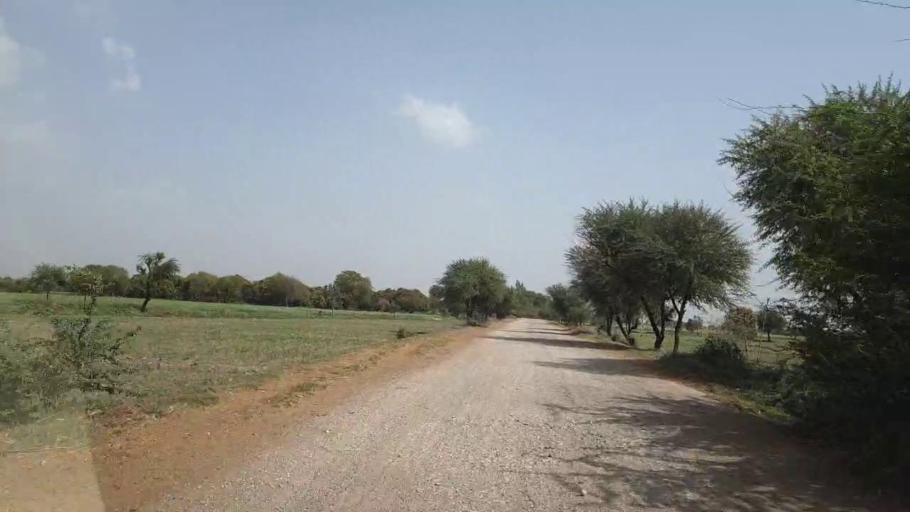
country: PK
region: Sindh
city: Rajo Khanani
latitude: 25.0511
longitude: 68.8614
